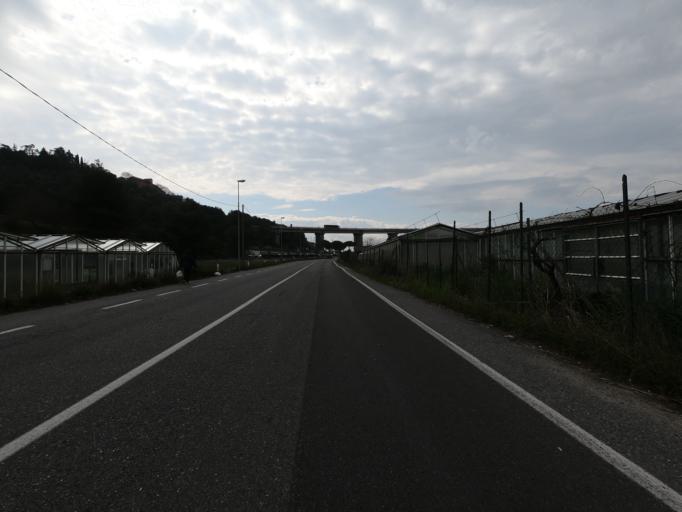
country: IT
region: Liguria
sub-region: Provincia di Savona
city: Andora
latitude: 43.9680
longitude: 8.1411
